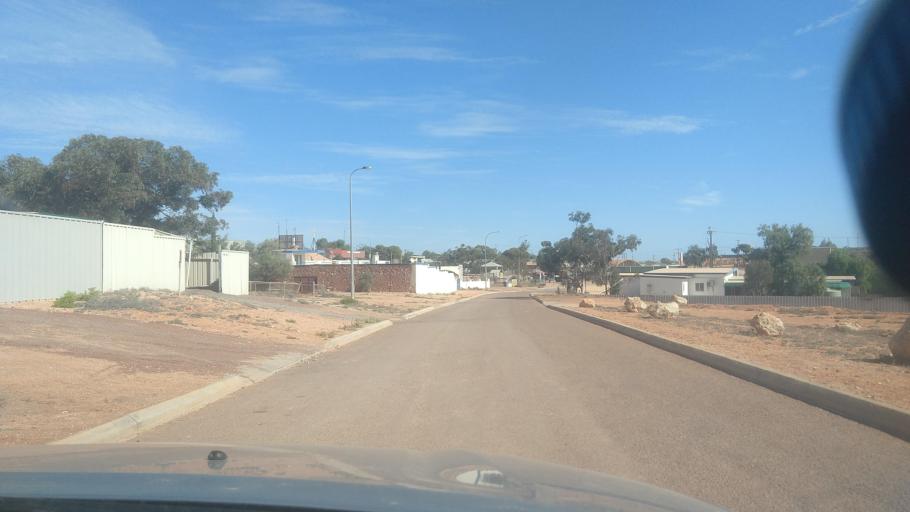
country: AU
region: South Australia
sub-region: Coober Pedy
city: Coober Pedy
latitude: -29.0117
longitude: 134.7566
